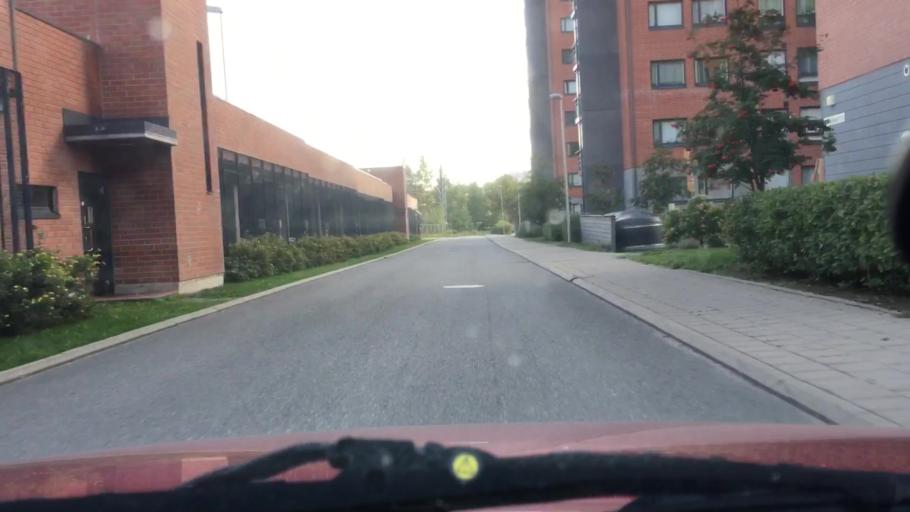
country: FI
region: Varsinais-Suomi
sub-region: Turku
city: Turku
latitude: 60.4540
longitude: 22.2485
